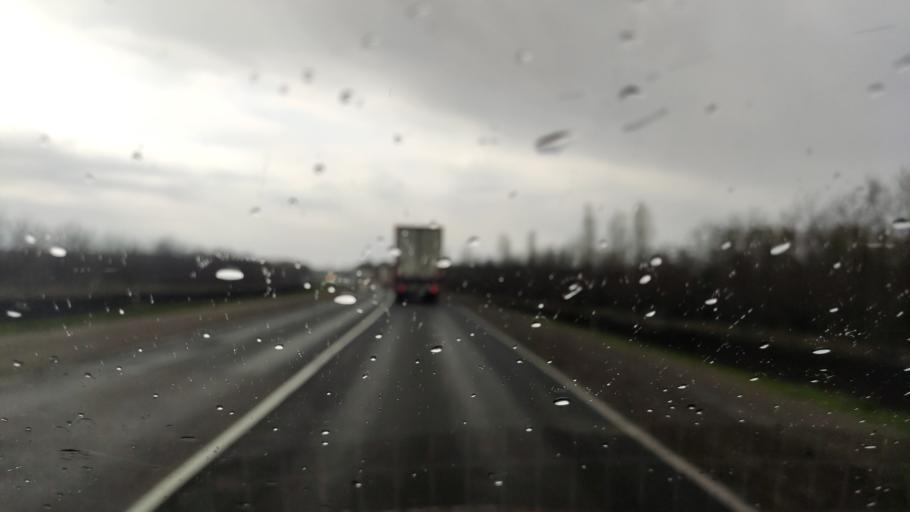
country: RU
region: Voronezj
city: Nizhnedevitsk
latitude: 51.5734
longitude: 38.3292
